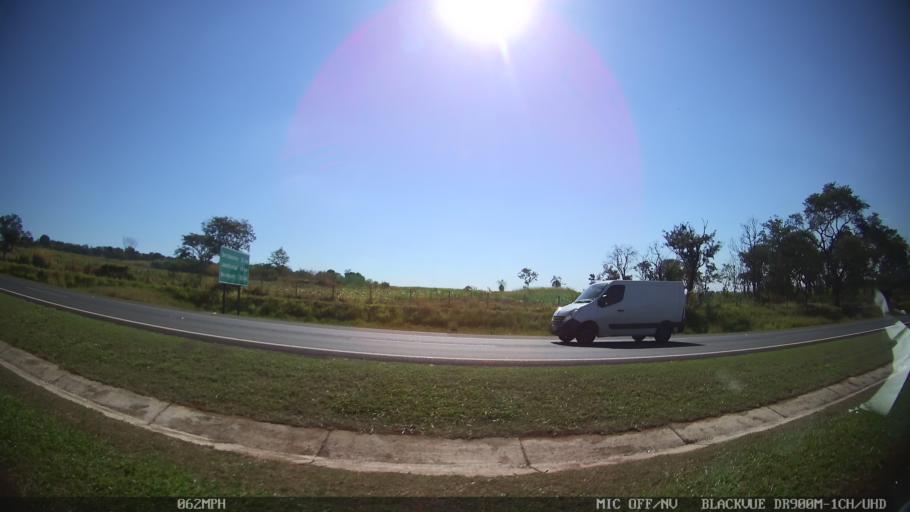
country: BR
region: Sao Paulo
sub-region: Ribeirao Preto
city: Ribeirao Preto
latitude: -21.1104
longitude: -47.8164
